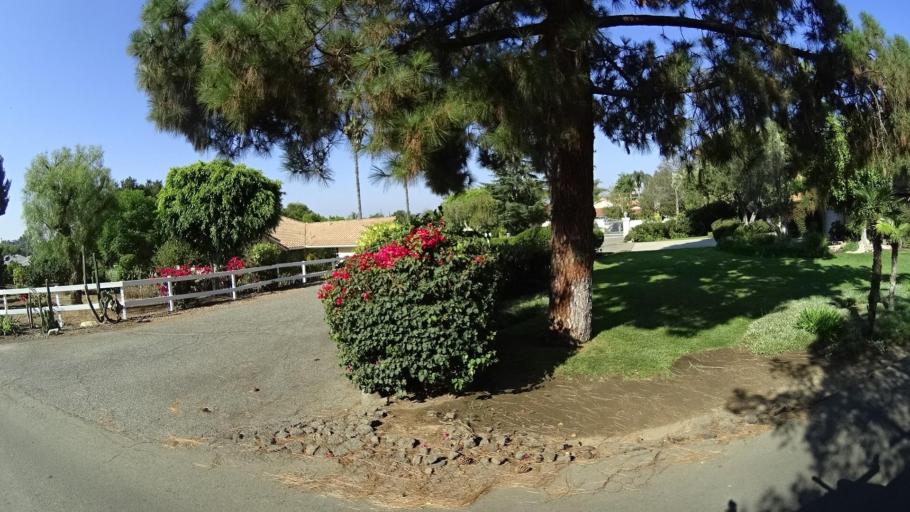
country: US
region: California
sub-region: San Diego County
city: Fallbrook
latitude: 33.3926
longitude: -117.2281
